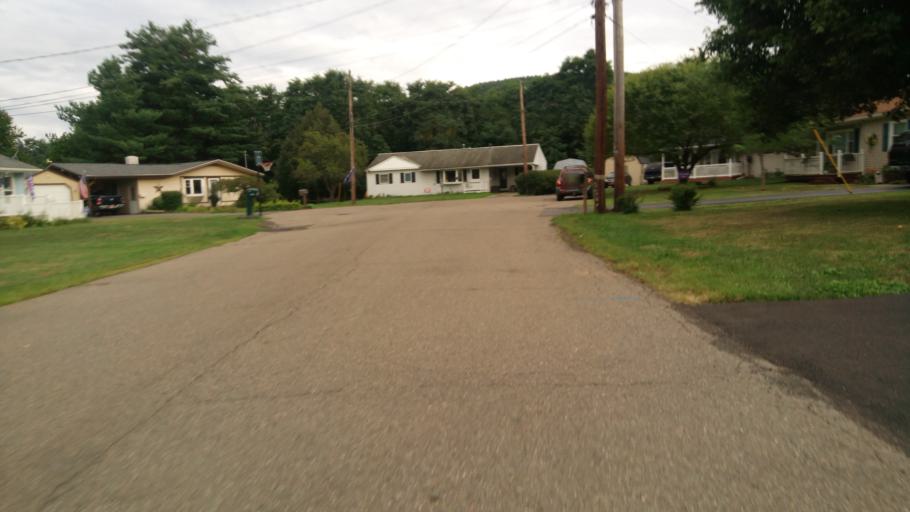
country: US
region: New York
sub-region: Chemung County
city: Southport
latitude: 42.0580
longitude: -76.8132
